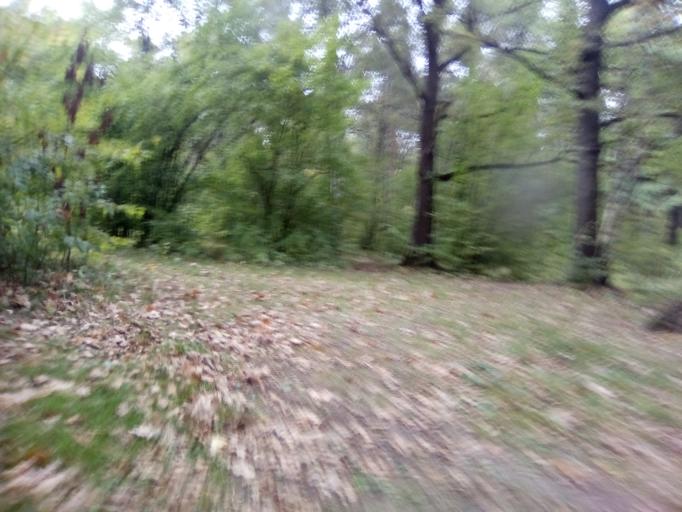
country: RU
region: Moskovskaya
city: Kokoshkino
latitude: 55.6122
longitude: 37.1894
